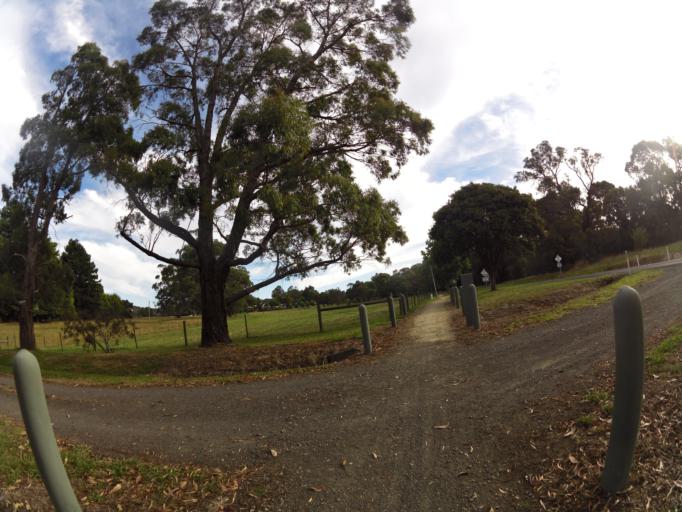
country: AU
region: Victoria
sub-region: Colac-Otway
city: Colac
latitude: -38.5119
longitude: 143.7165
